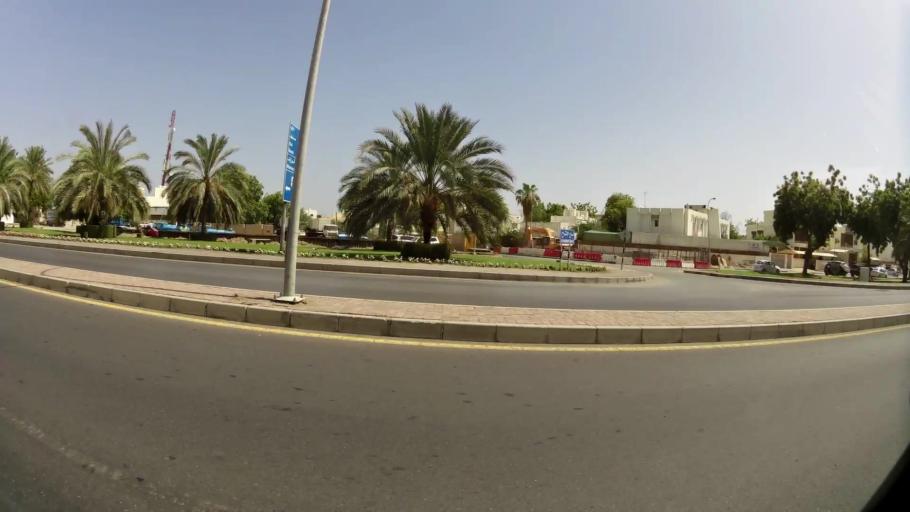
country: OM
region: Muhafazat Masqat
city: Bawshar
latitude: 23.5972
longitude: 58.4462
